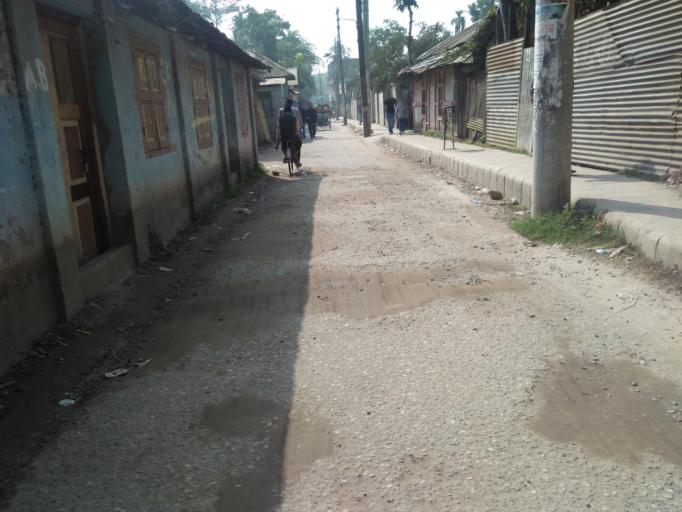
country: BD
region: Barisal
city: Bhola
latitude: 22.6844
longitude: 90.6427
